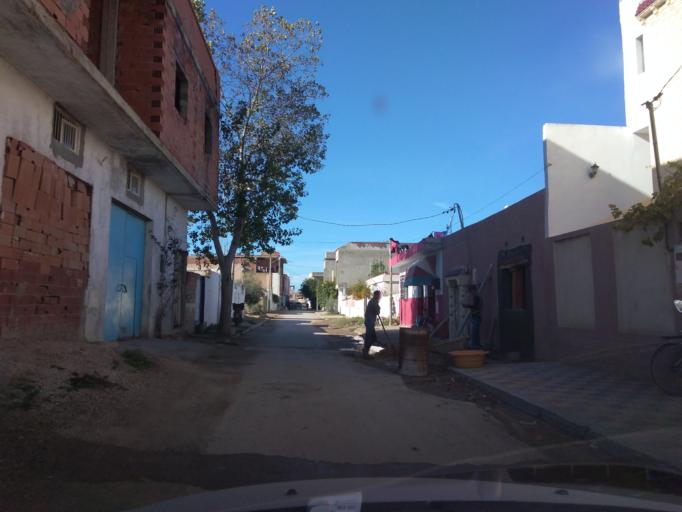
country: TN
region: Ariana
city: Qal'at al Andalus
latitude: 37.0650
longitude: 10.1232
